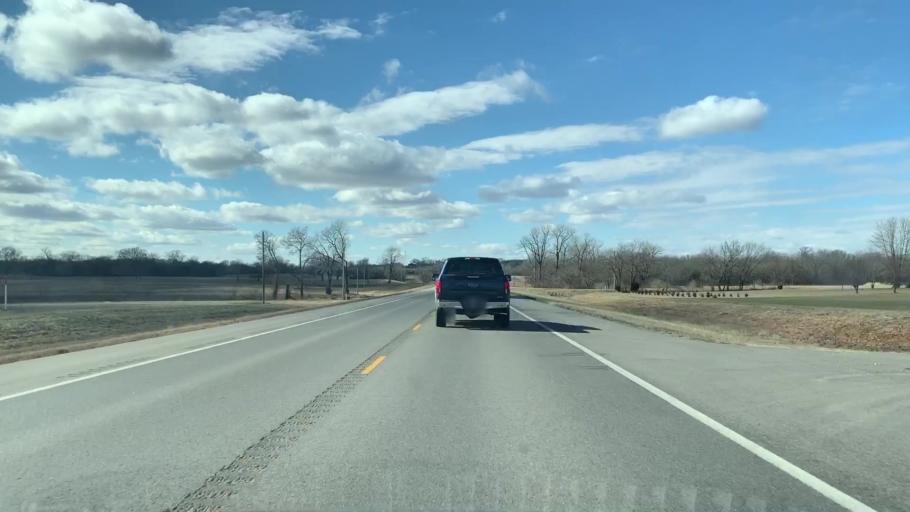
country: US
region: Kansas
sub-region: Cherokee County
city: Columbus
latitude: 37.3400
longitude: -94.8824
